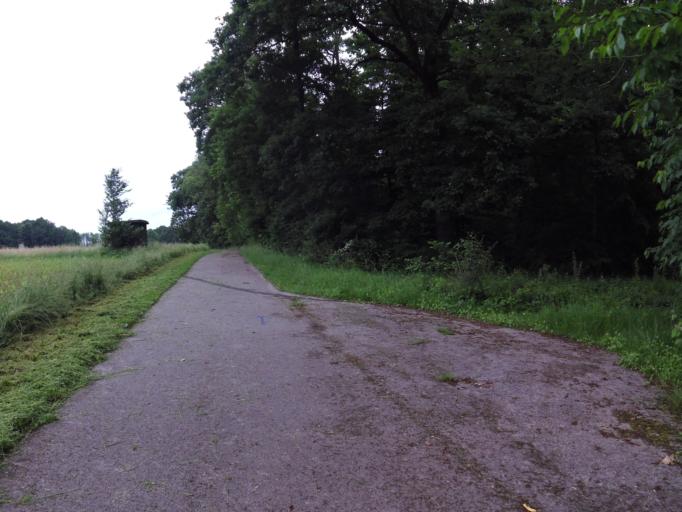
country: FR
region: Champagne-Ardenne
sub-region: Departement de la Haute-Marne
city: Montier-en-Der
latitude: 48.5434
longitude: 4.7684
